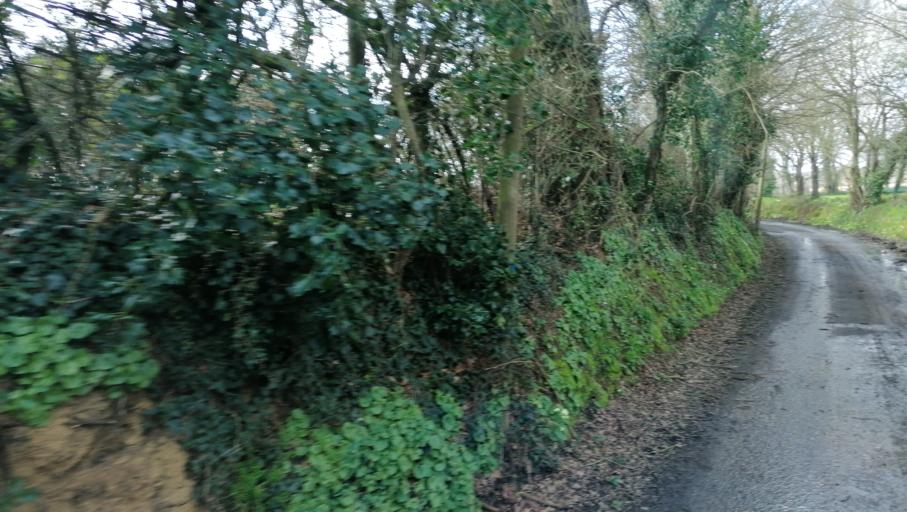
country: FR
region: Brittany
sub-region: Departement des Cotes-d'Armor
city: Pleguien
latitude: 48.6399
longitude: -2.9305
